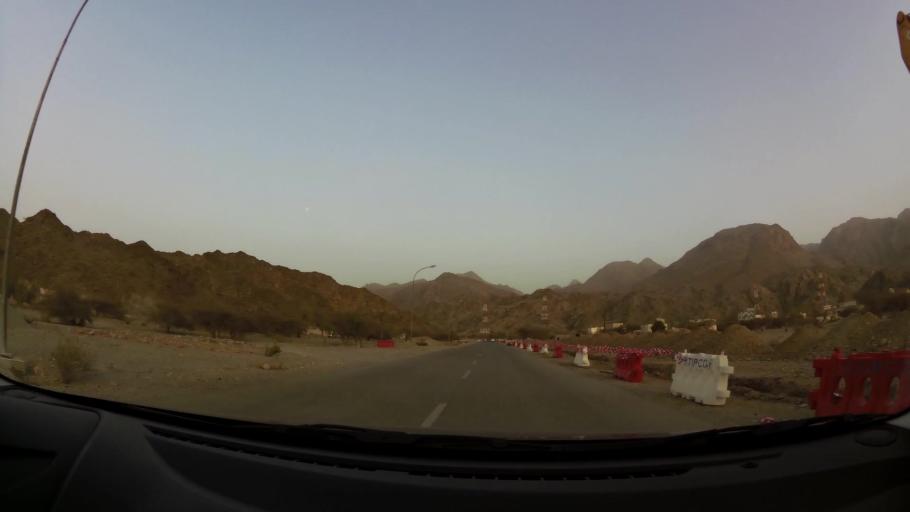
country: OM
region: Muhafazat Masqat
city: Bawshar
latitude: 23.4737
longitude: 58.3091
